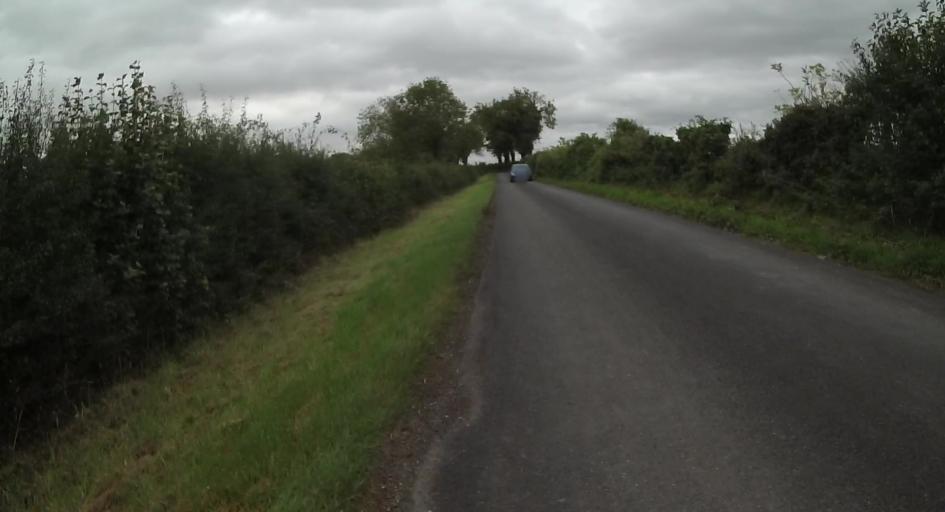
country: GB
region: England
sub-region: Hampshire
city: Four Marks
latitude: 51.1536
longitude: -1.1175
